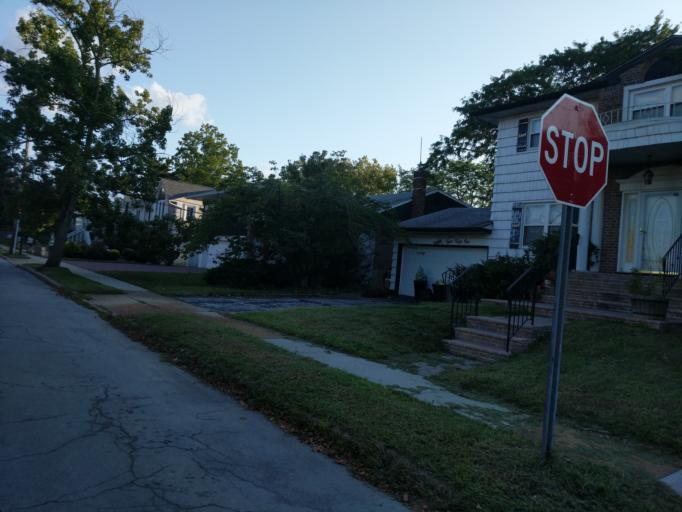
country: US
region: New York
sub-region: Nassau County
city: South Valley Stream
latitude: 40.6450
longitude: -73.7346
